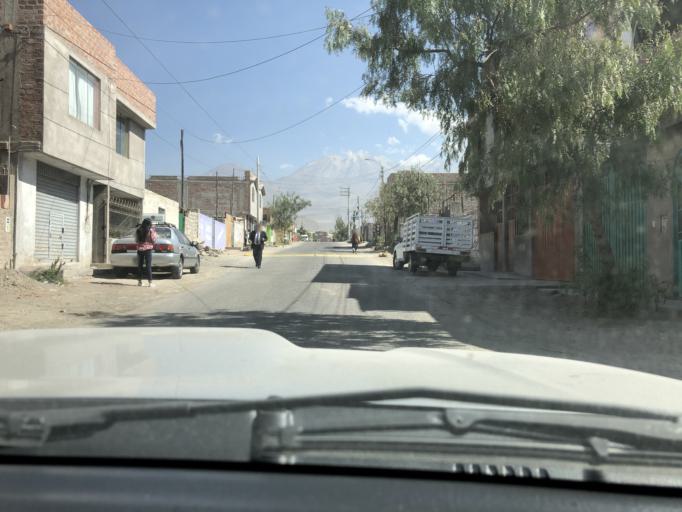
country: PE
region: Arequipa
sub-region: Provincia de Arequipa
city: Arequipa
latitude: -16.3428
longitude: -71.5520
